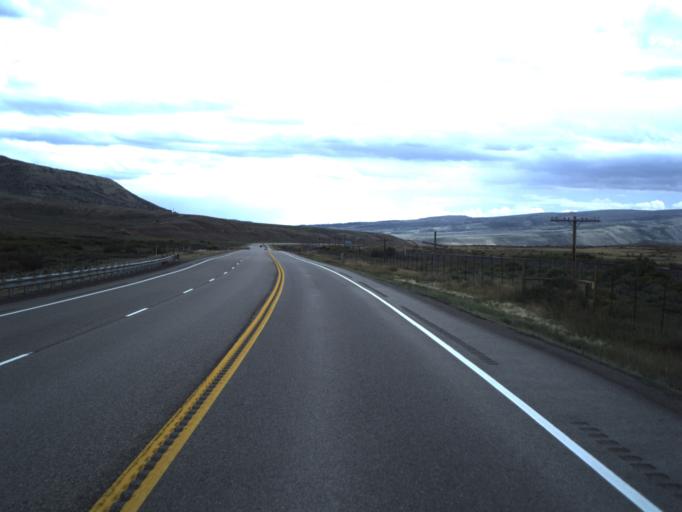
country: US
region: Utah
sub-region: Carbon County
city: Helper
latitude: 39.8835
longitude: -111.0474
